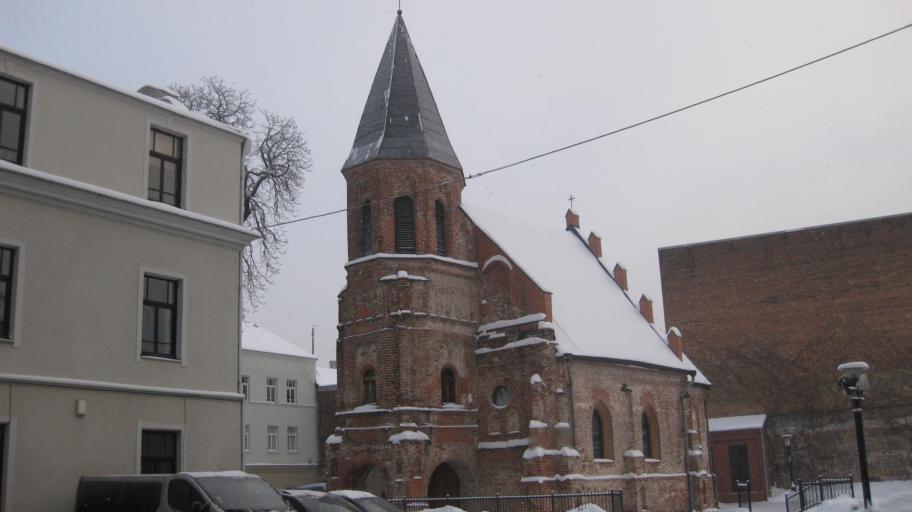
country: LT
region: Kauno apskritis
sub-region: Kaunas
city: Kaunas
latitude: 54.8972
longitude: 23.9011
